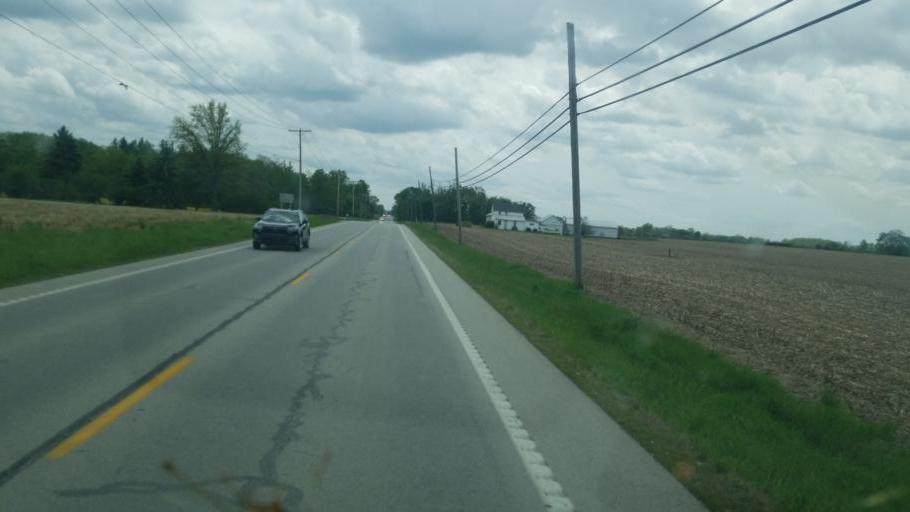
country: US
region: Ohio
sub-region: Seneca County
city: Tiffin
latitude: 41.1648
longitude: -83.1684
